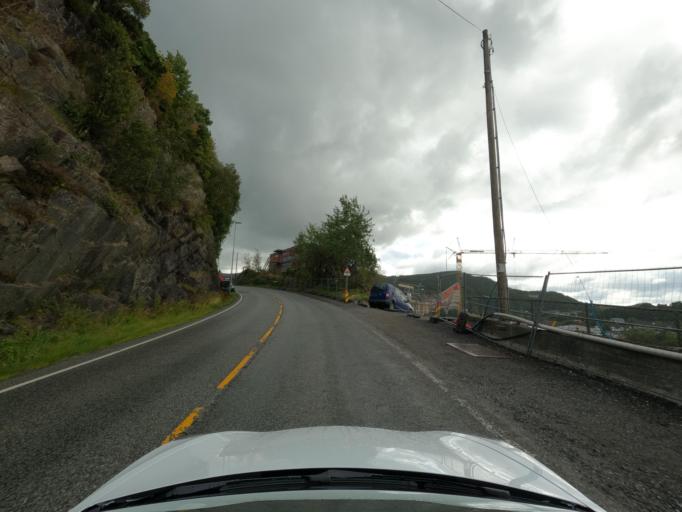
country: NO
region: Hordaland
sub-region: Bergen
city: Hylkje
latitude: 60.4711
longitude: 5.3444
